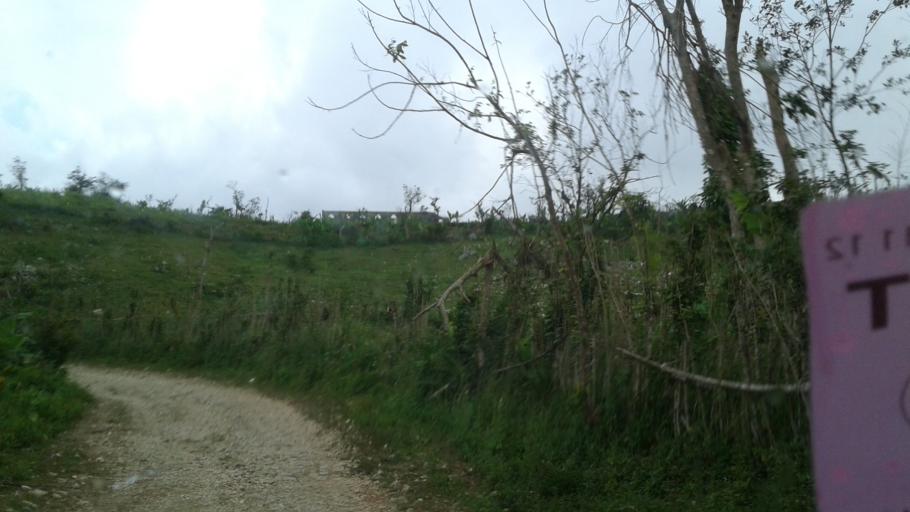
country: HT
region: Grandans
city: Jeremie
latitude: 18.4944
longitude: -74.1100
